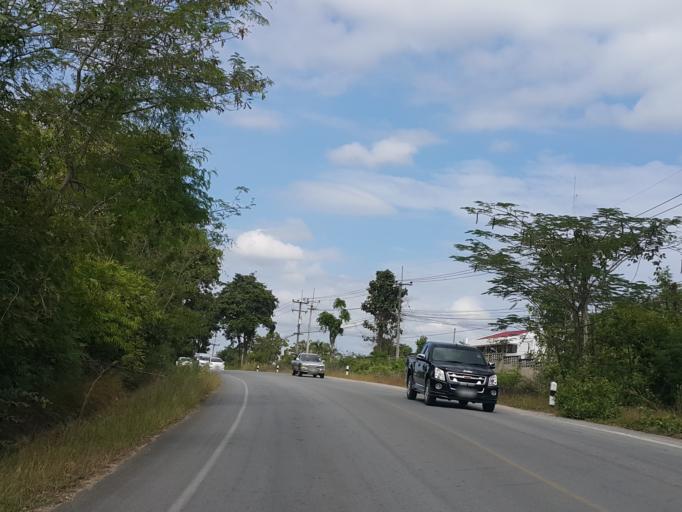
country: TH
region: Lampang
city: Lampang
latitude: 18.4095
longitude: 99.4525
